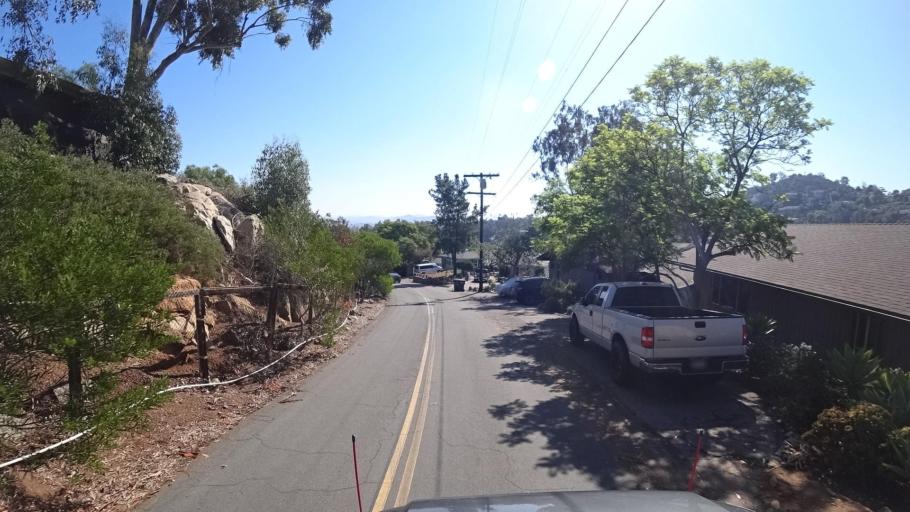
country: US
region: California
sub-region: San Diego County
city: Casa de Oro-Mount Helix
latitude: 32.7740
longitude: -116.9876
